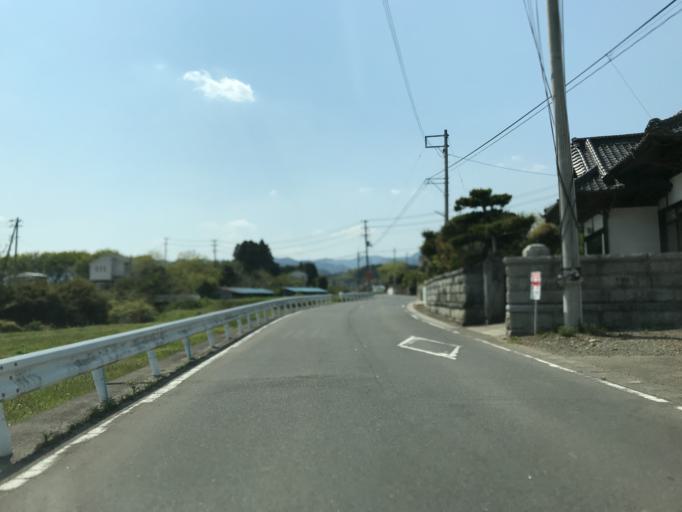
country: JP
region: Ibaraki
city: Kitaibaraki
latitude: 36.8962
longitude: 140.7599
